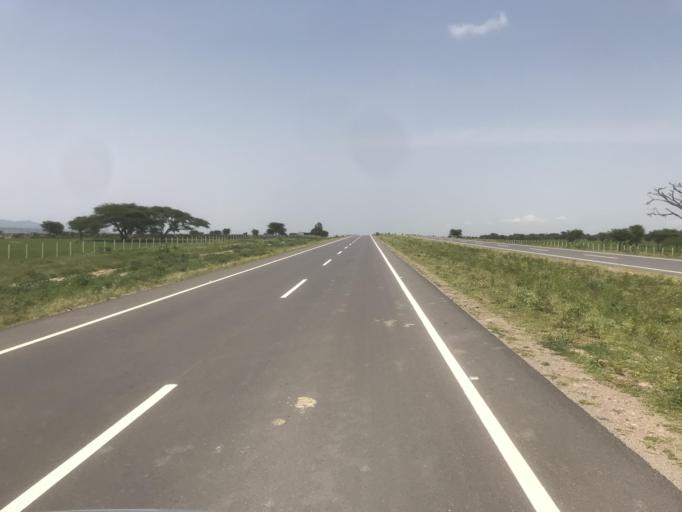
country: ET
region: Oromiya
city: Mojo
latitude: 8.3654
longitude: 38.9933
